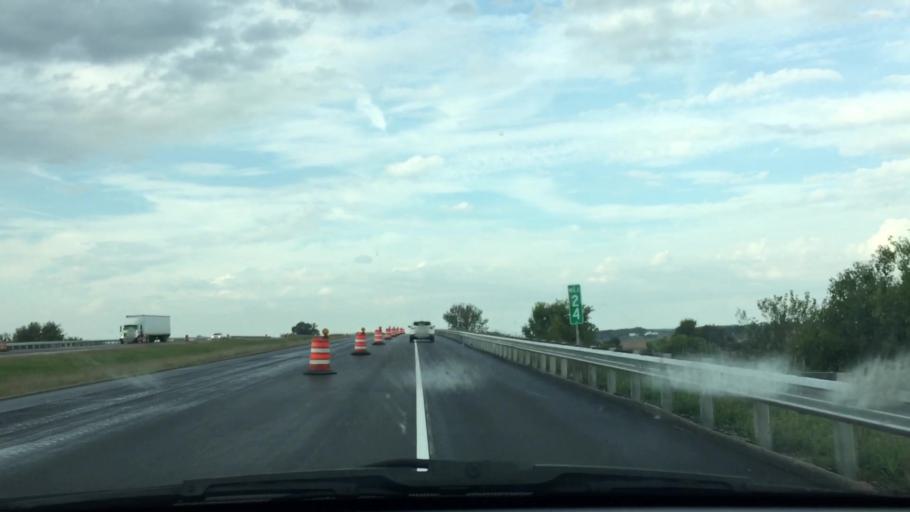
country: US
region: Illinois
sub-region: Whiteside County
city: Prophetstown
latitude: 41.7149
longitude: -89.9990
